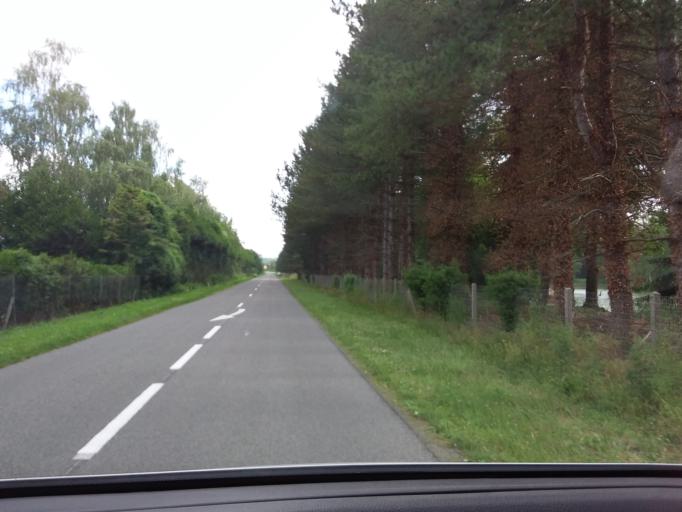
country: FR
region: Champagne-Ardenne
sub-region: Departement de la Marne
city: Fismes
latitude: 49.3810
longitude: 3.6492
